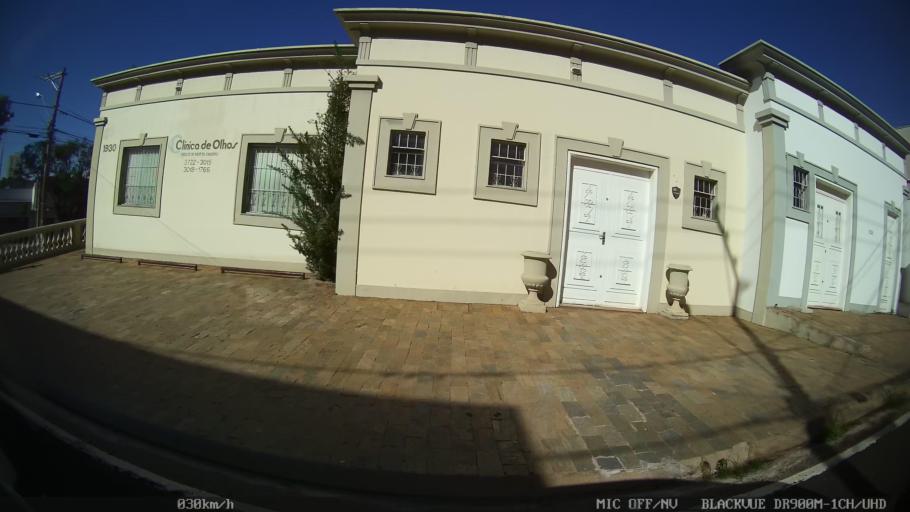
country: BR
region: Sao Paulo
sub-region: Franca
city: Franca
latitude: -20.5428
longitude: -47.3986
